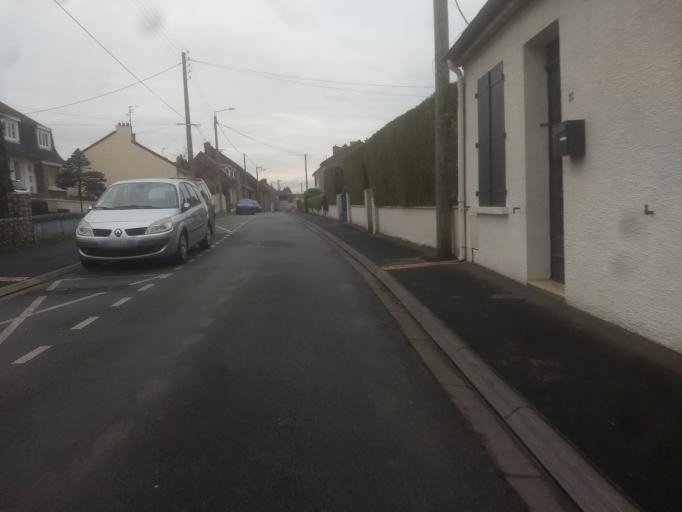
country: FR
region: Nord-Pas-de-Calais
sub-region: Departement du Pas-de-Calais
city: Agny
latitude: 50.2631
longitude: 2.7595
